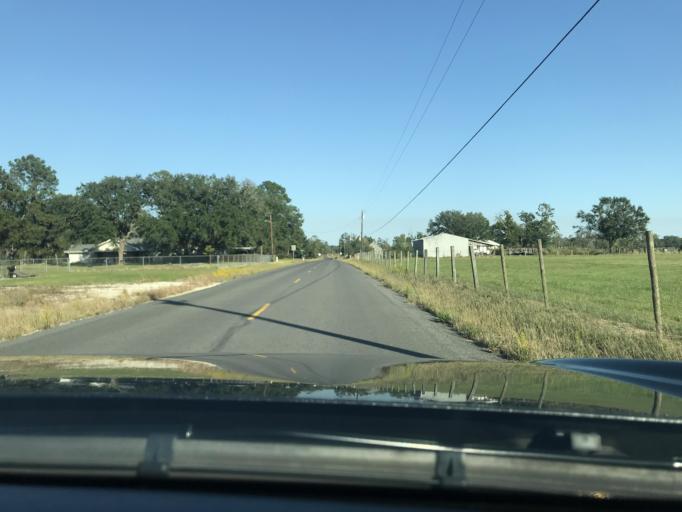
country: US
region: Louisiana
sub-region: Calcasieu Parish
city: Westlake
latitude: 30.3153
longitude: -93.2705
